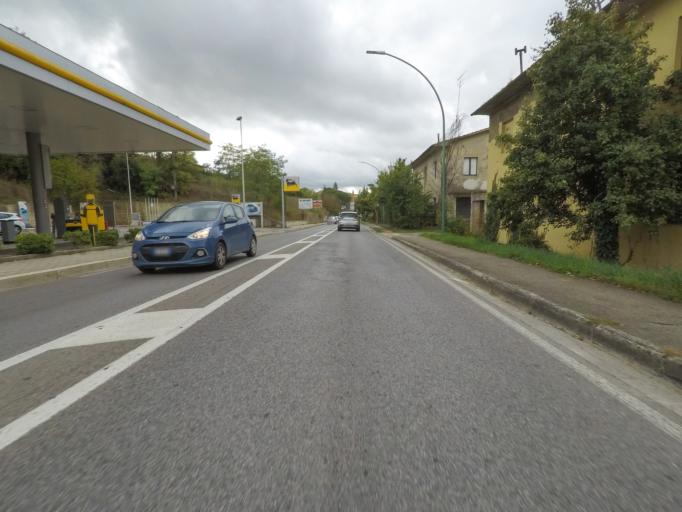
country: IT
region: Tuscany
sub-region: Provincia di Siena
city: Siena
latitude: 43.3223
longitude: 11.3482
